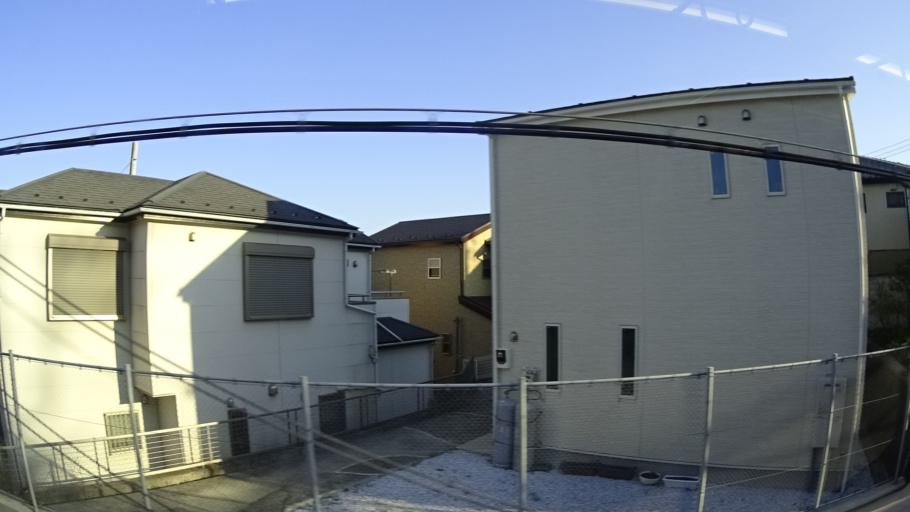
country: JP
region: Kanagawa
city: Yokosuka
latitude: 35.2063
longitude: 139.6765
